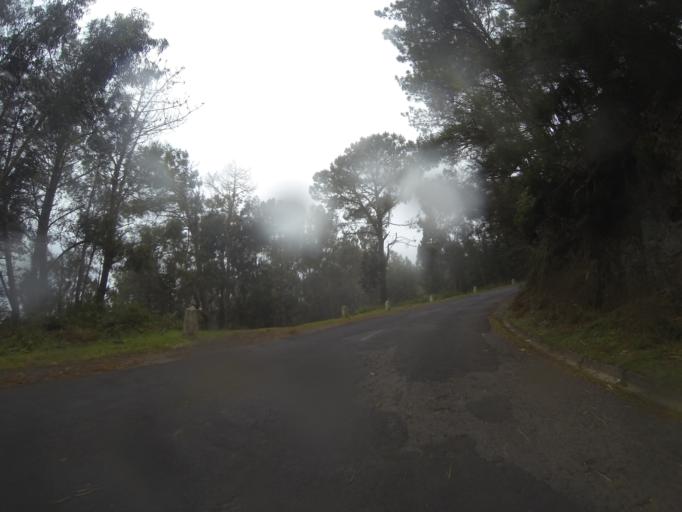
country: PT
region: Madeira
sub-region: Calheta
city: Estreito da Calheta
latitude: 32.7776
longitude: -17.1896
